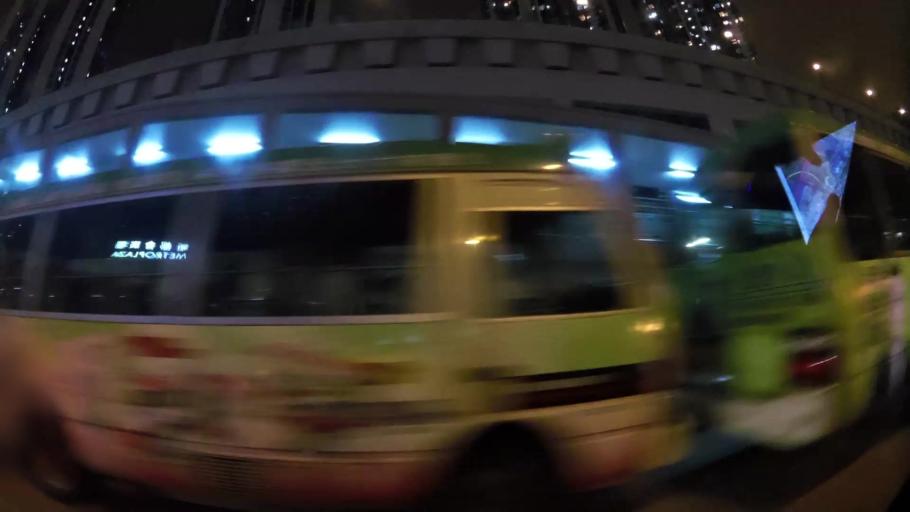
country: HK
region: Tsuen Wan
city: Tsuen Wan
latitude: 22.3568
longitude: 114.1276
